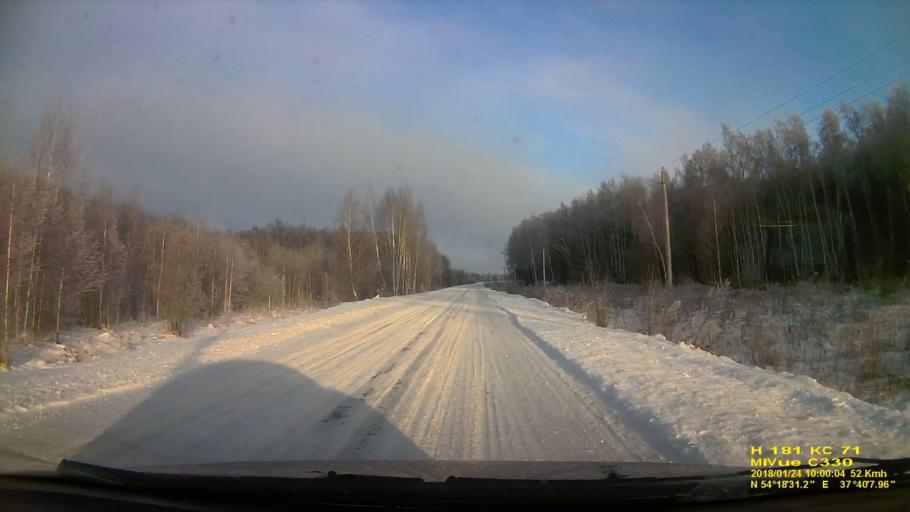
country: RU
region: Tula
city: Revyakino
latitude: 54.3087
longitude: 37.6688
